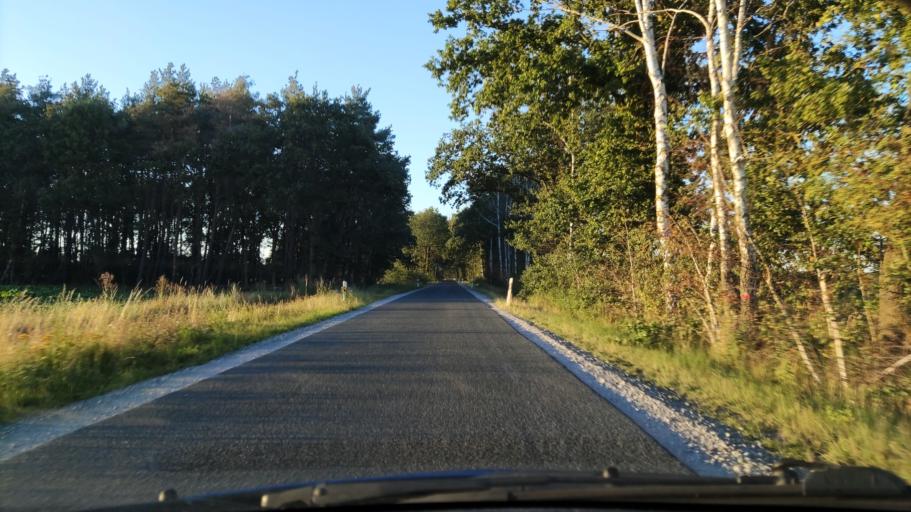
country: DE
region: Lower Saxony
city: Klein Gusborn
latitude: 53.0664
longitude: 11.1875
